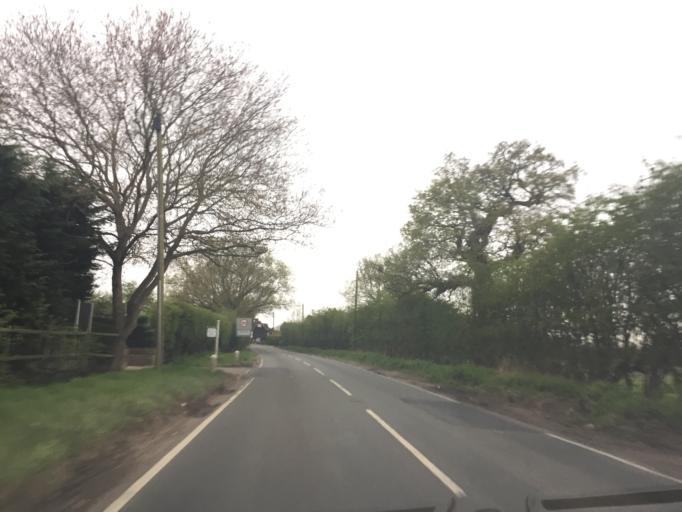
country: GB
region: England
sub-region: Essex
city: Theydon Bois
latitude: 51.6551
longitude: 0.1262
